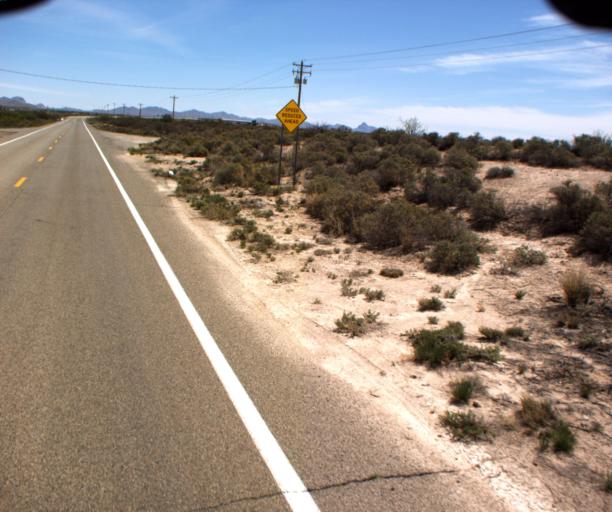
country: US
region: New Mexico
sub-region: Hidalgo County
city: Lordsburg
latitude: 32.2608
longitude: -109.2025
